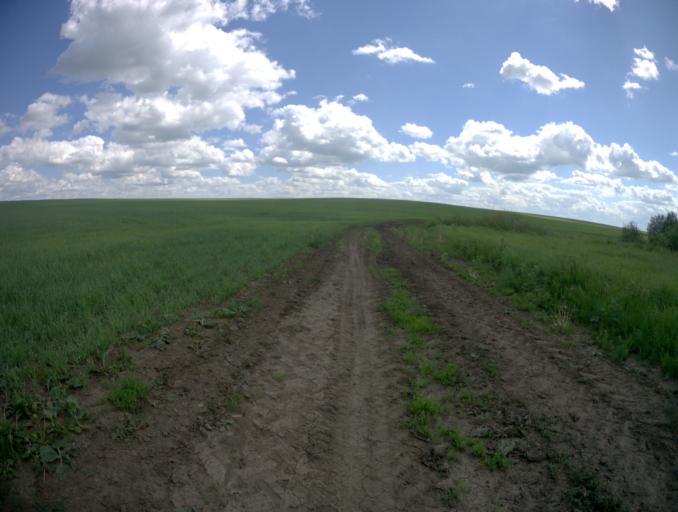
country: RU
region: Vladimir
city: Suzdal'
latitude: 56.4369
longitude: 40.2824
